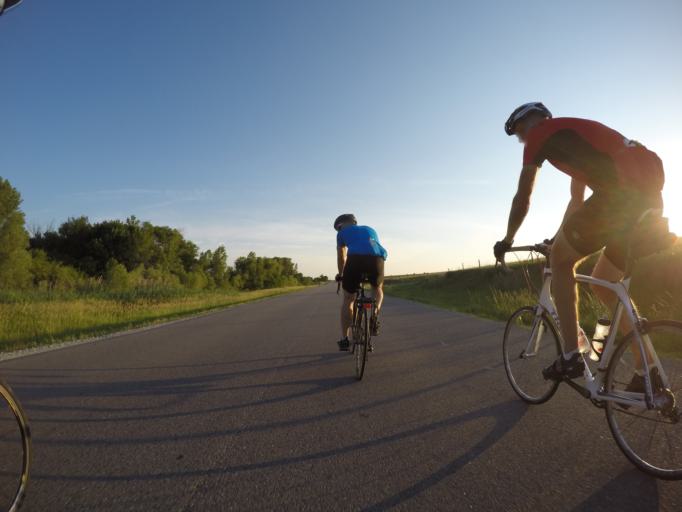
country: US
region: Kansas
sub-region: Marshall County
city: Marysville
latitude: 39.8443
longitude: -96.6009
